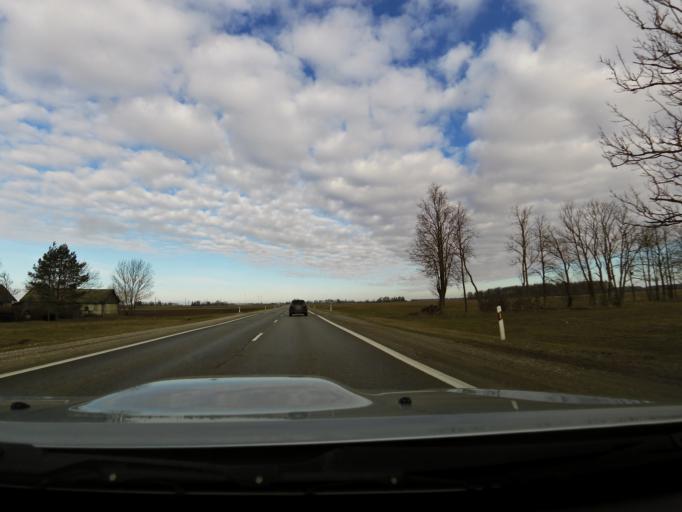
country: LT
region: Siauliu apskritis
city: Pakruojis
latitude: 55.7756
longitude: 24.0542
